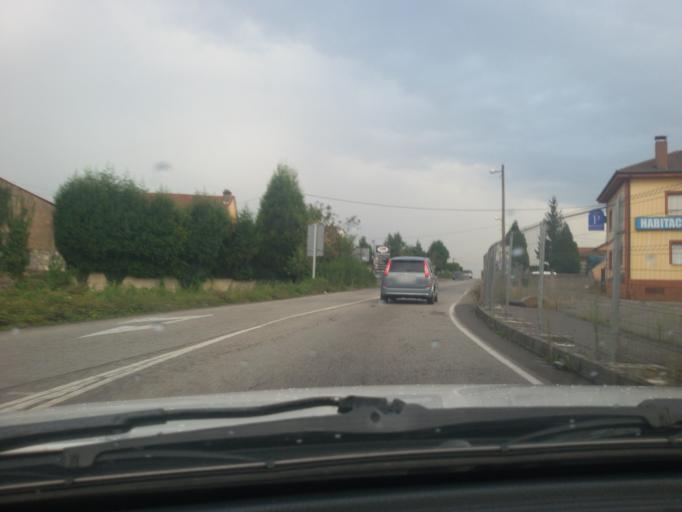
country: ES
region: Asturias
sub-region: Province of Asturias
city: Lugones
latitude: 43.3991
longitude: -5.7909
